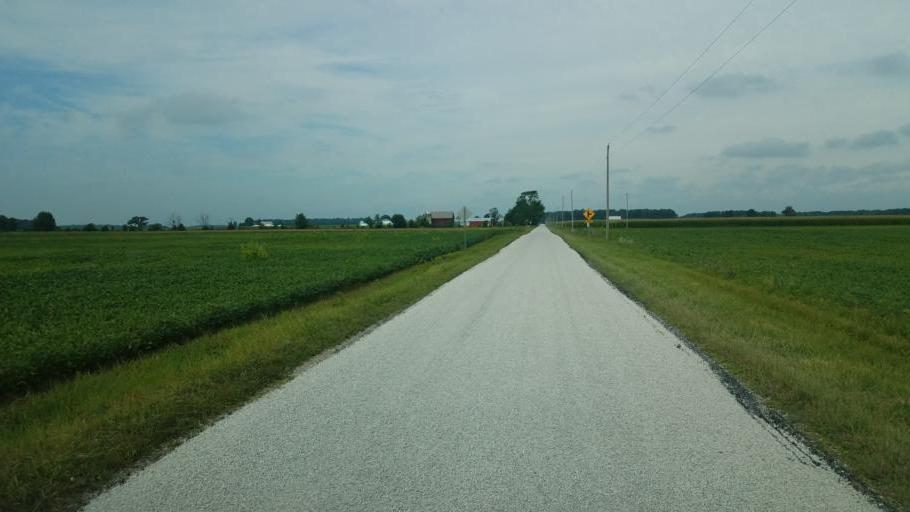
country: US
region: Ohio
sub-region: Morrow County
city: Cardington
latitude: 40.5139
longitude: -82.9836
